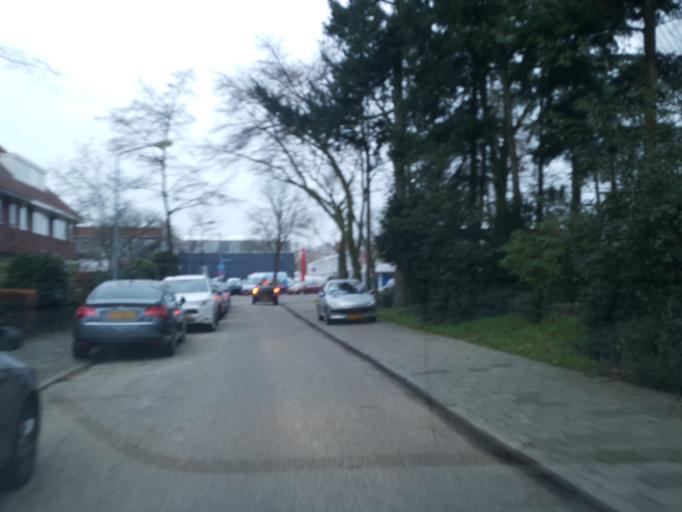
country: NL
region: North Holland
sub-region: Gemeente Wijdemeren
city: Nieuw-Loosdrecht
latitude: 52.2183
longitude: 5.1504
